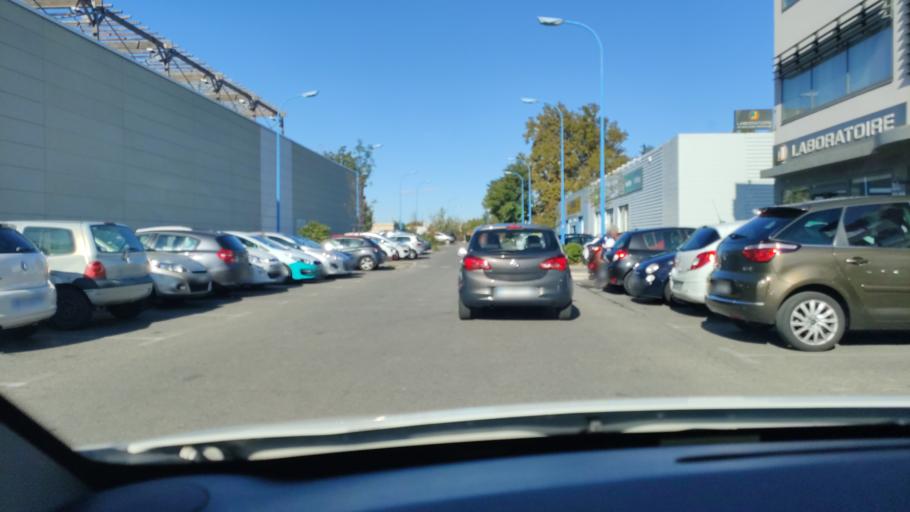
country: FR
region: Provence-Alpes-Cote d'Azur
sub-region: Departement du Vaucluse
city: Le Pontet
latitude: 43.9517
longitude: 4.8601
